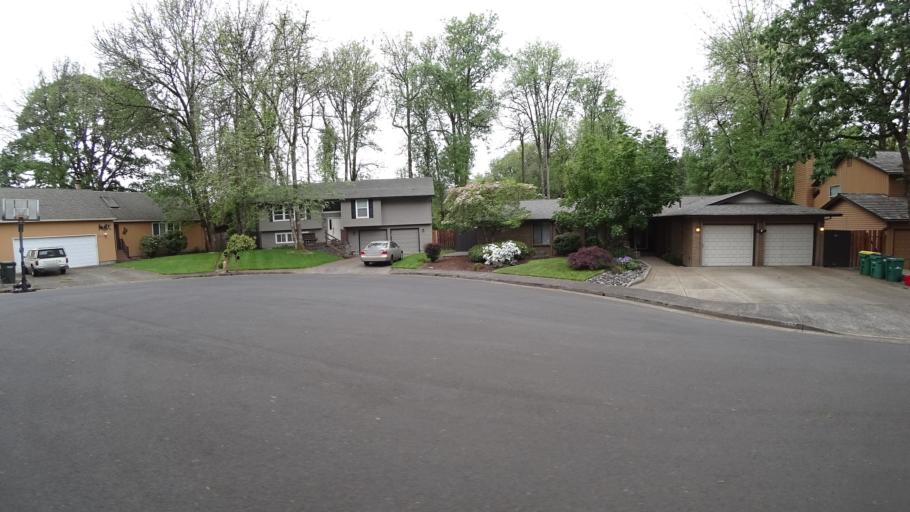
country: US
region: Oregon
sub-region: Washington County
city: Beaverton
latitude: 45.4697
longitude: -122.8059
